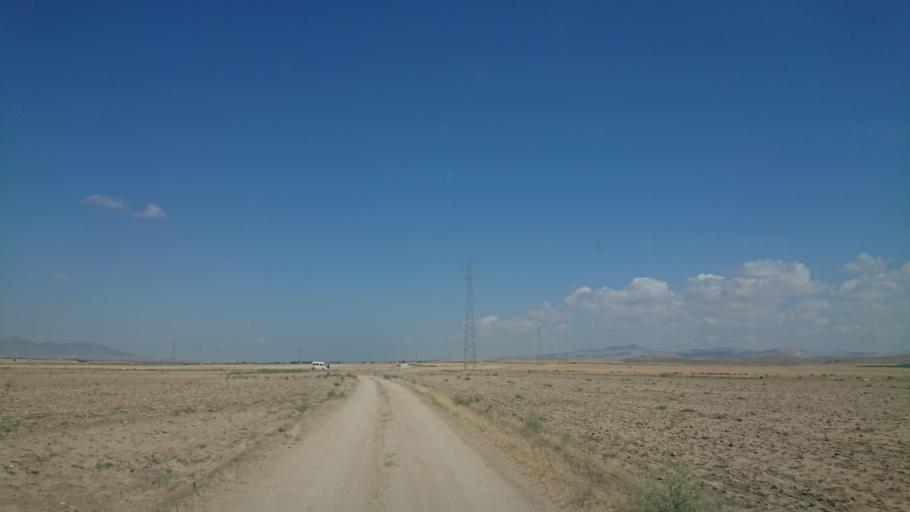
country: TR
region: Aksaray
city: Sariyahsi
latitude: 39.0004
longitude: 33.8908
